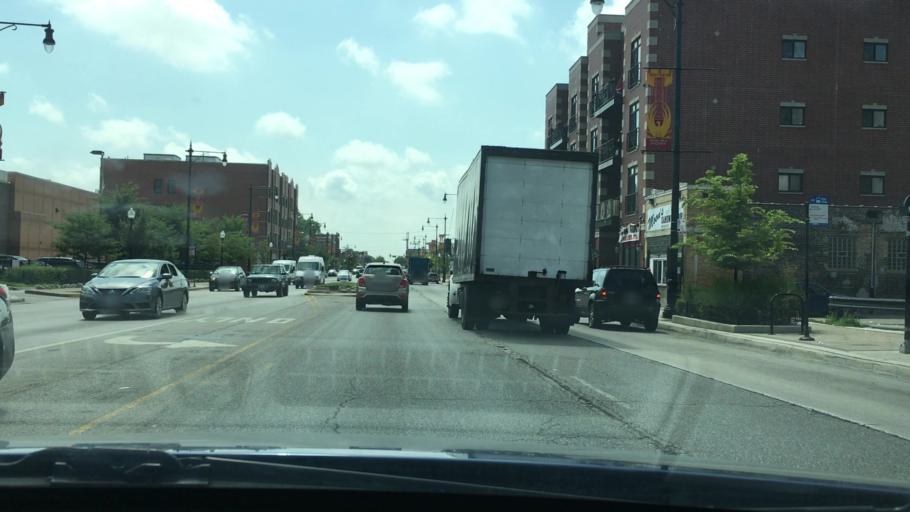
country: US
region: Illinois
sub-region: Cook County
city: Chicago
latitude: 41.8810
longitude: -87.6865
